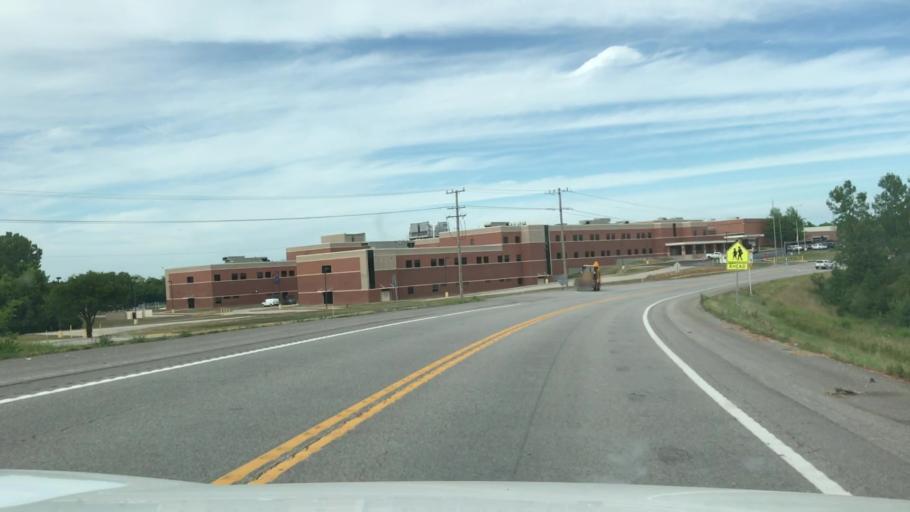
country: US
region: Missouri
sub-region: Saint Charles County
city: Weldon Spring
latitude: 38.7005
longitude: -90.7192
